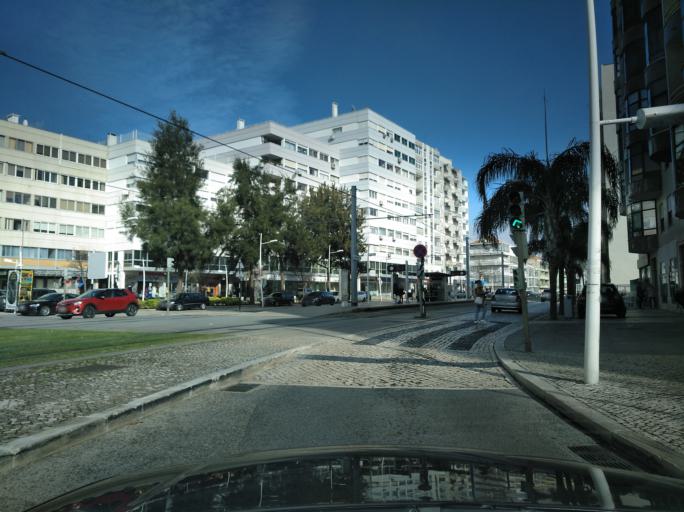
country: PT
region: Setubal
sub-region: Almada
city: Pragal
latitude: 38.6763
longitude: -9.1647
